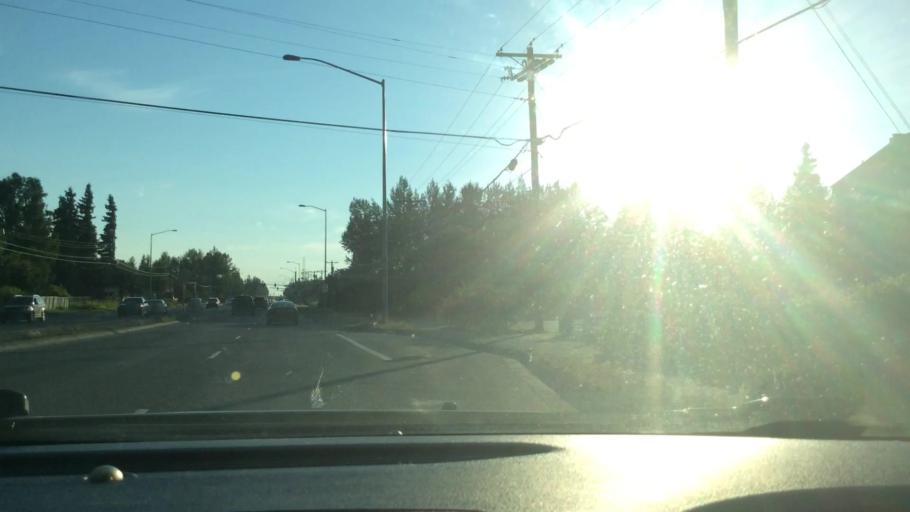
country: US
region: Alaska
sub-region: Anchorage Municipality
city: Elmendorf Air Force Base
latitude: 61.2095
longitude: -149.7569
